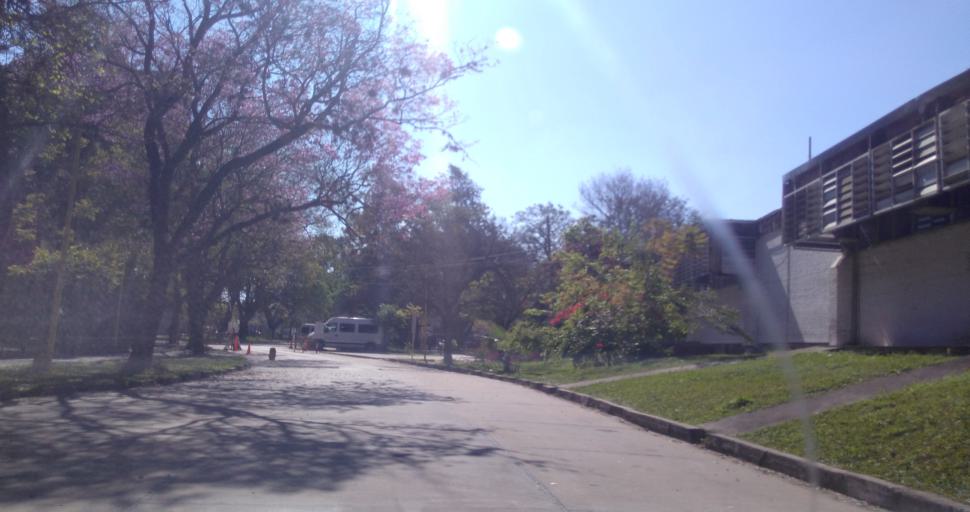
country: AR
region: Chaco
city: Resistencia
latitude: -27.4635
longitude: -58.9840
